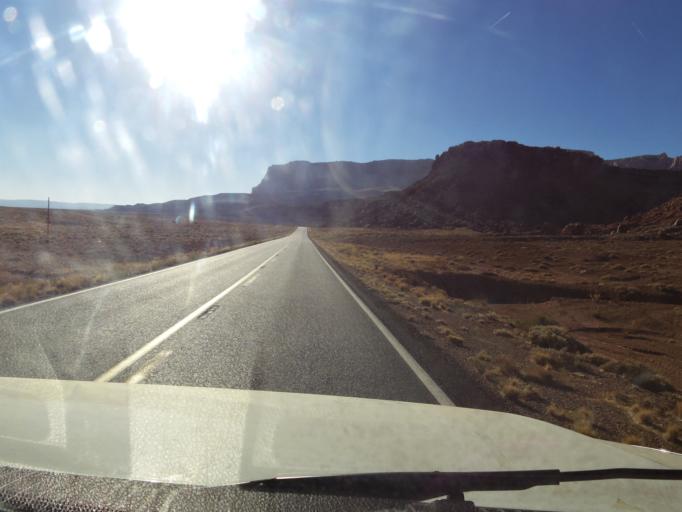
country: US
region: Arizona
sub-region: Coconino County
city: Page
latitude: 36.7488
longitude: -111.7363
